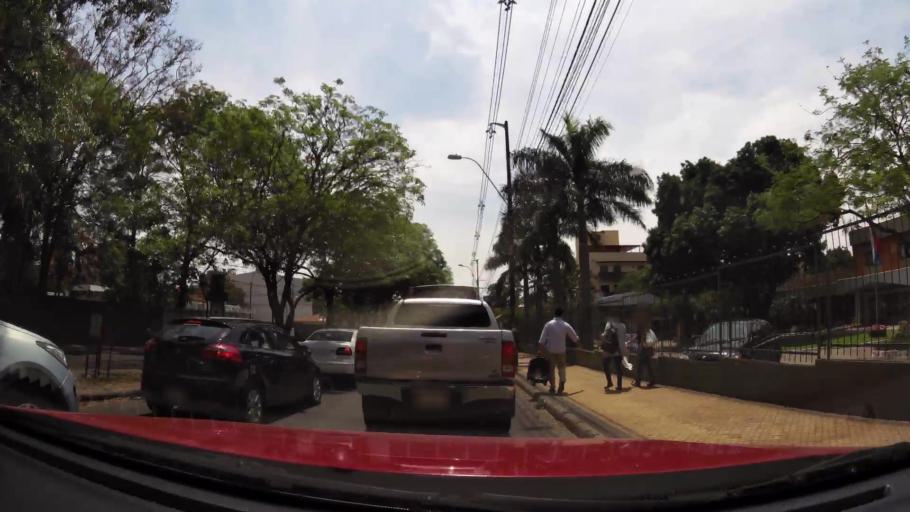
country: PY
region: Central
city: Lambare
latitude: -25.2990
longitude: -57.5793
